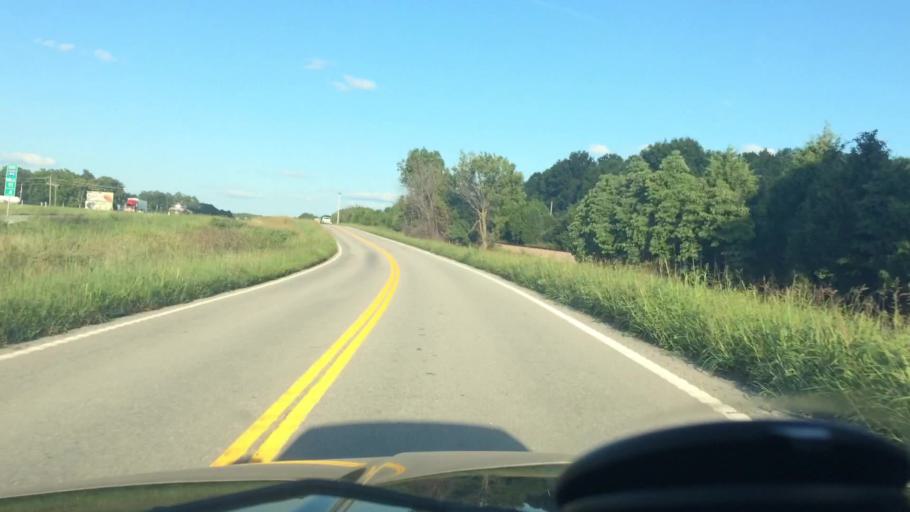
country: US
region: Missouri
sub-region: Greene County
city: Strafford
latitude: 37.2699
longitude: -93.0700
